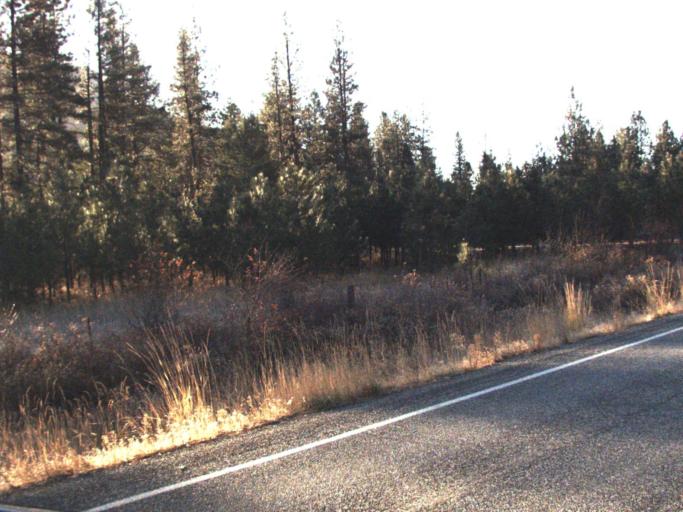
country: US
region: Washington
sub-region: Okanogan County
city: Coulee Dam
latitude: 48.2062
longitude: -118.7128
